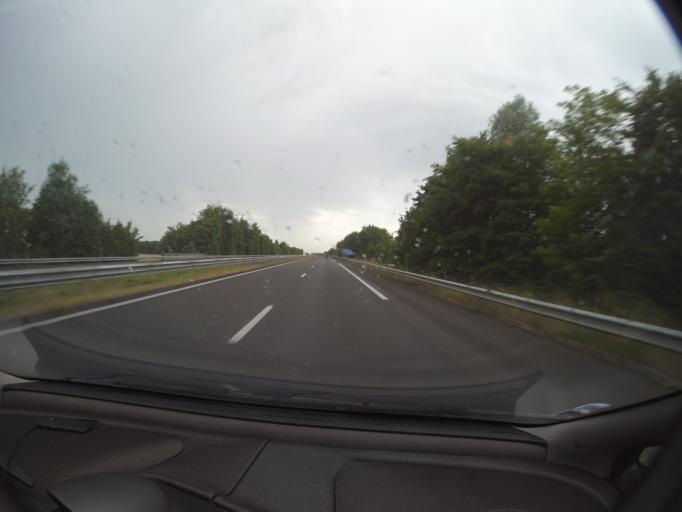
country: FR
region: Pays de la Loire
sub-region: Departement de la Sarthe
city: Parce-sur-Sarthe
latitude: 47.8258
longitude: -0.1484
